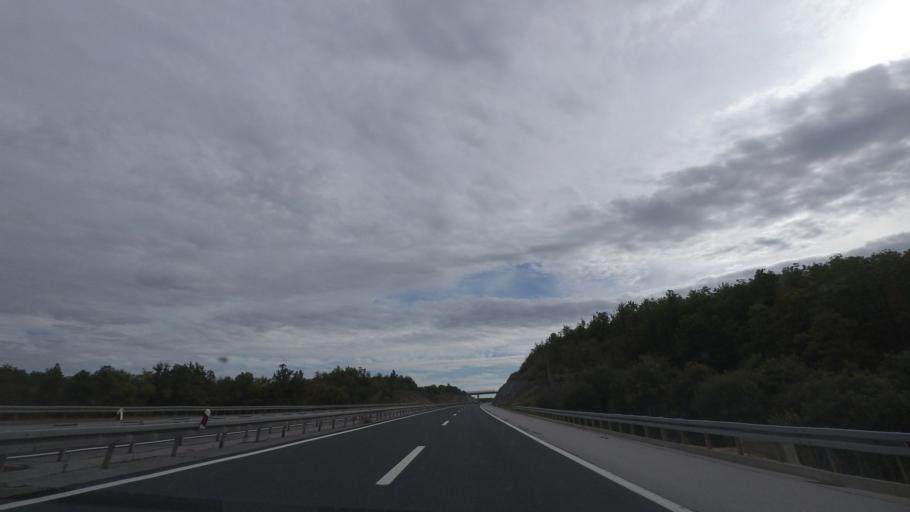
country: HR
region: Licko-Senjska
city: Gospic
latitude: 44.7245
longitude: 15.3857
